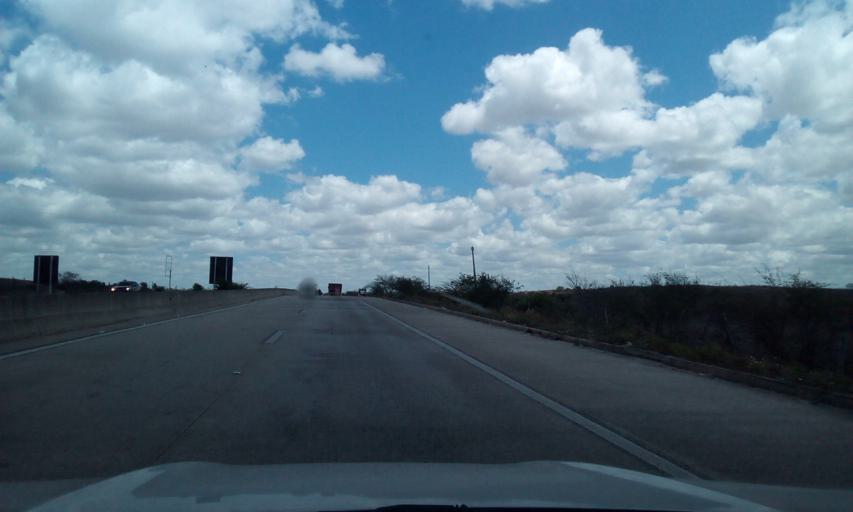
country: BR
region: Alagoas
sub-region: Porto Real Do Colegio
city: Porto Real do Colegio
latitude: -10.1772
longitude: -36.8258
